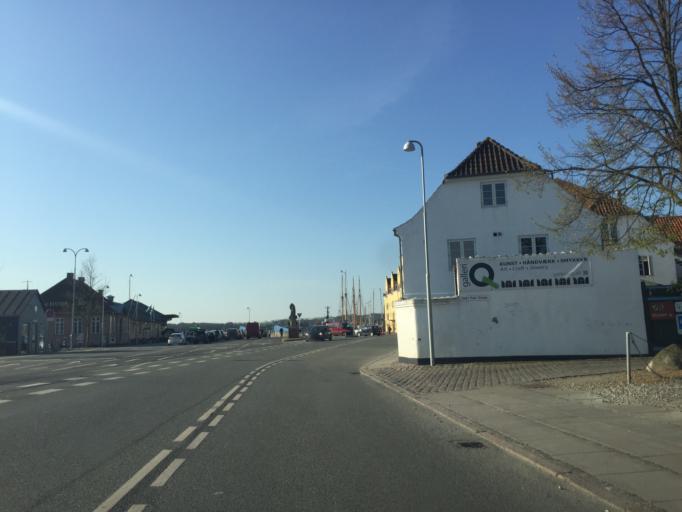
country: DK
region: South Denmark
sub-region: Svendborg Kommune
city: Svendborg
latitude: 55.0588
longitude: 10.6142
